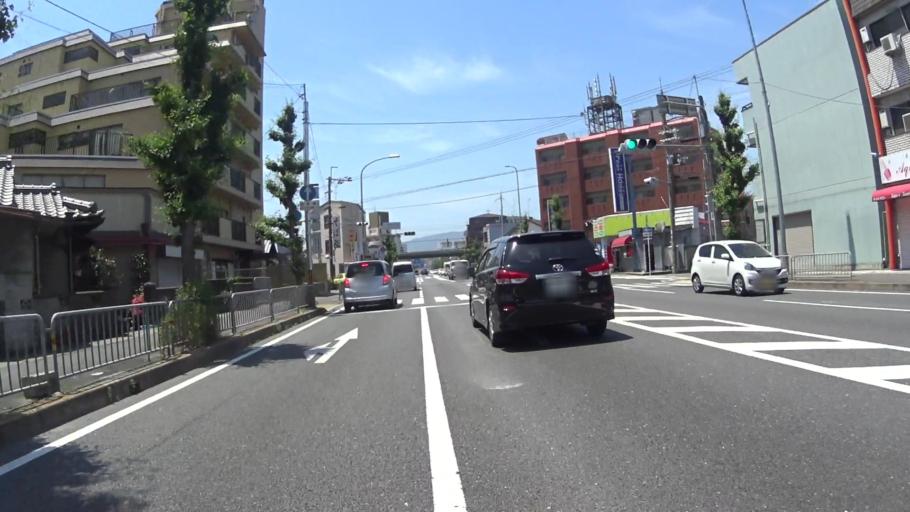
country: JP
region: Kyoto
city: Kameoka
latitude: 35.0334
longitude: 135.5512
